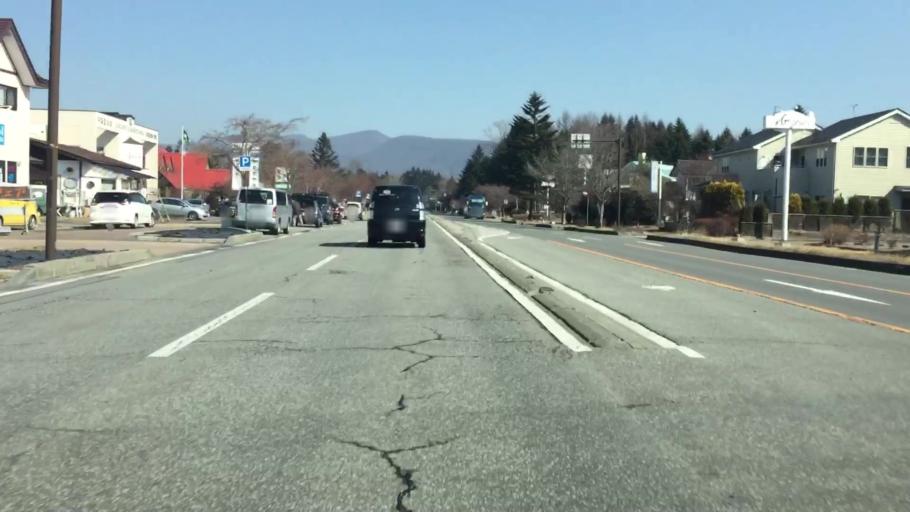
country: JP
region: Nagano
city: Saku
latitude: 36.3294
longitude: 138.6302
